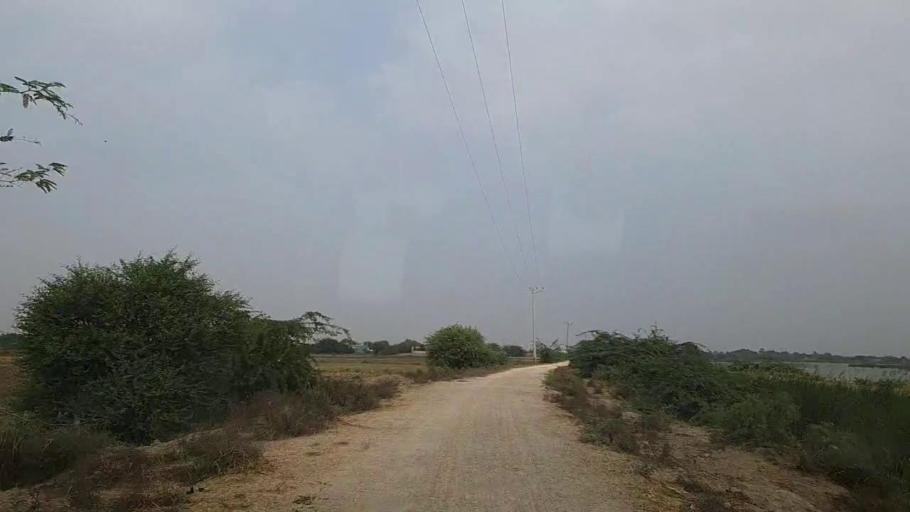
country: PK
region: Sindh
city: Mirpur Sakro
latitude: 24.6051
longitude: 67.7013
